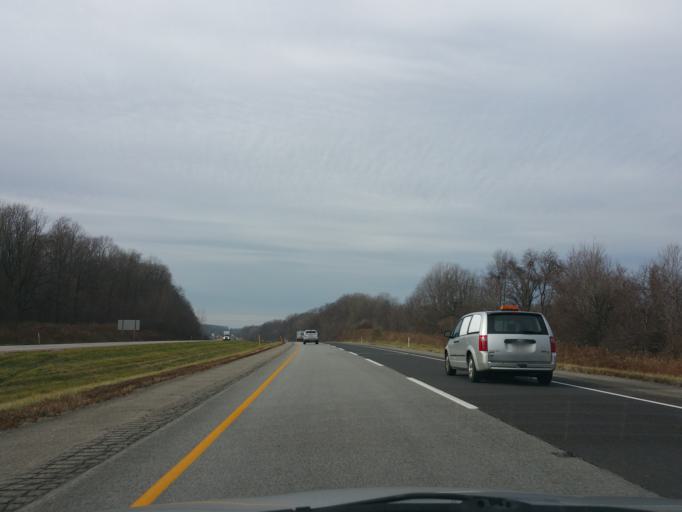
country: US
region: Indiana
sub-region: LaPorte County
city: Westville
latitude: 41.5842
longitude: -86.9393
